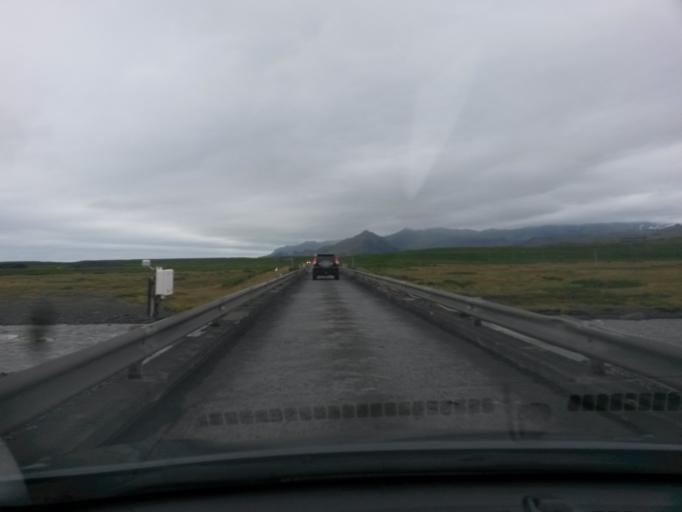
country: IS
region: South
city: Vestmannaeyjar
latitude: 63.4986
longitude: -19.4009
